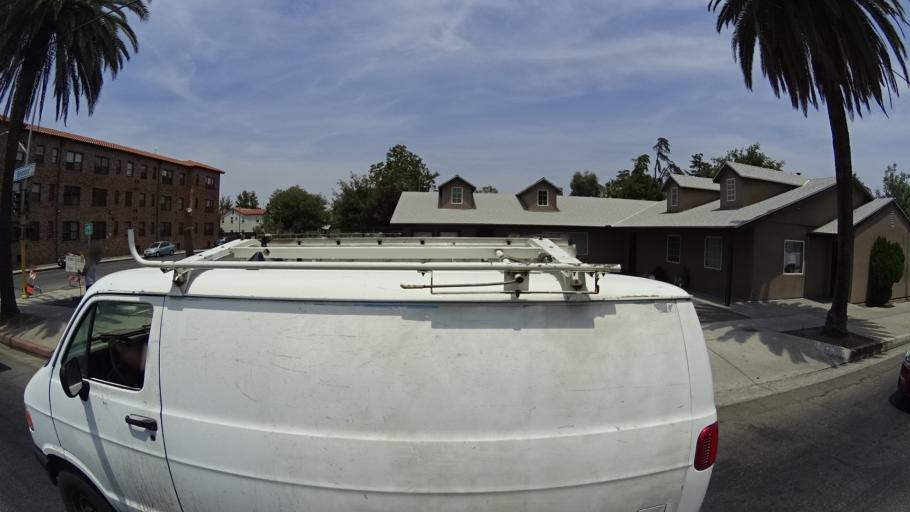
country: US
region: California
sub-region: Fresno County
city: Fresno
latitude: 36.7504
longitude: -119.8026
